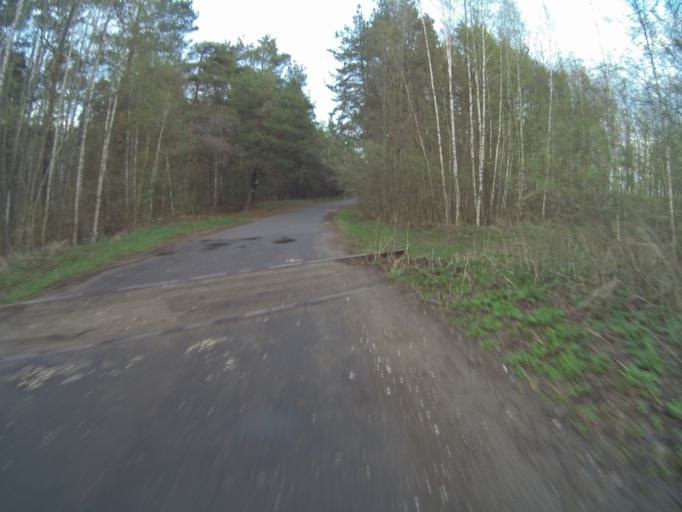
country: RU
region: Vladimir
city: Raduzhnyy
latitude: 56.0341
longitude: 40.3609
